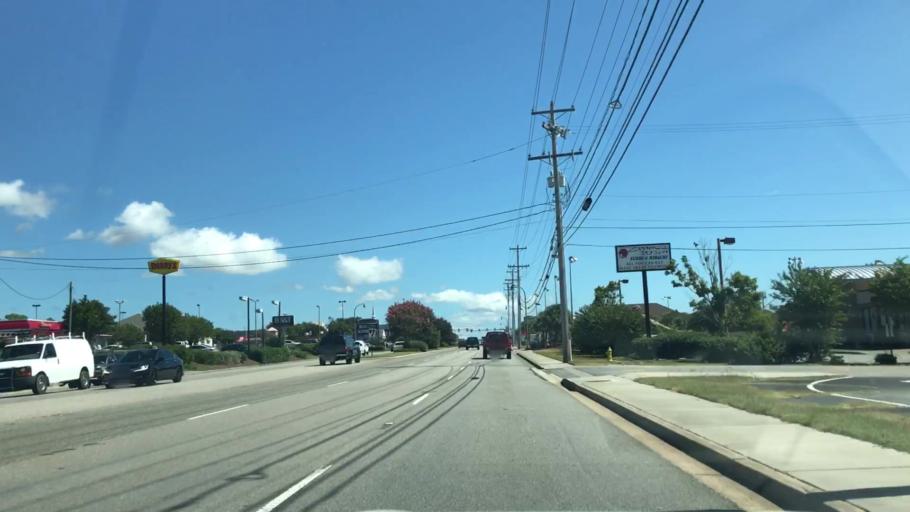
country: US
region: South Carolina
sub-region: Horry County
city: North Myrtle Beach
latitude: 33.8224
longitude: -78.6870
